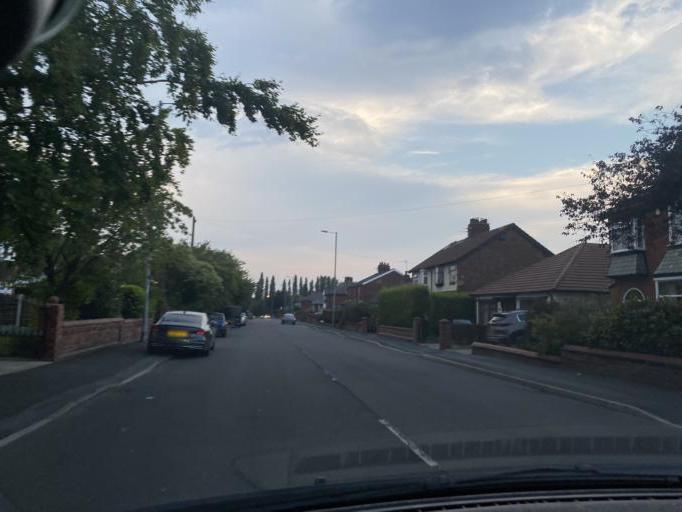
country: GB
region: England
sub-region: Borough of Tameside
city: Denton
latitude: 53.4700
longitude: -2.1226
